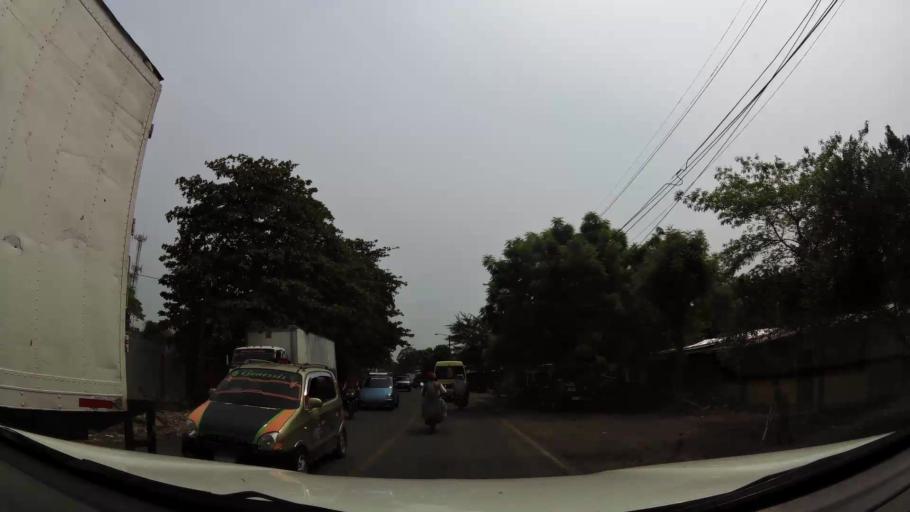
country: NI
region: Chinandega
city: Chinandega
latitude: 12.6396
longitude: -87.1311
